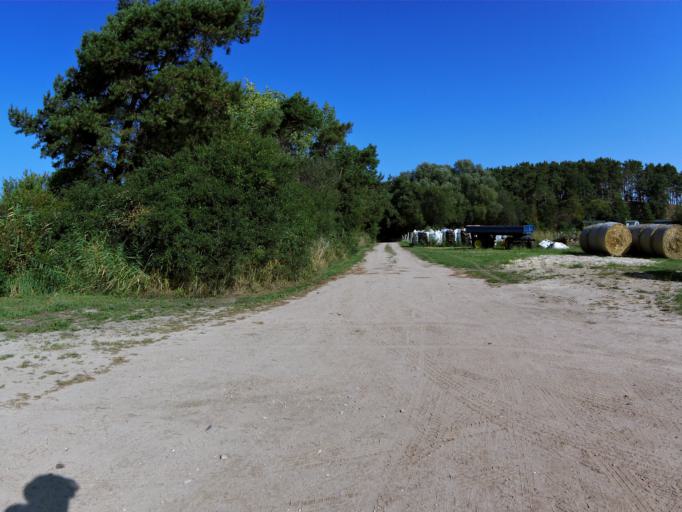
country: DE
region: Mecklenburg-Vorpommern
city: Loddin
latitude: 53.9636
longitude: 14.0442
